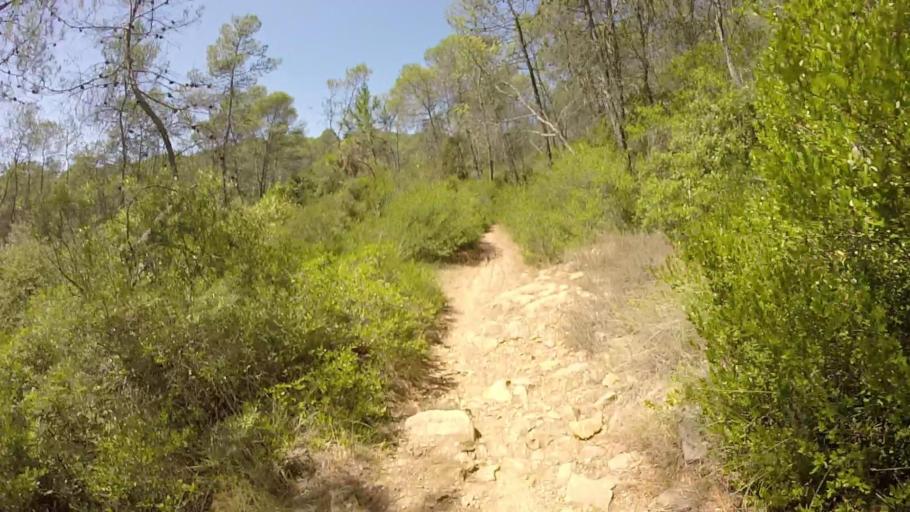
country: FR
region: Provence-Alpes-Cote d'Azur
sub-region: Departement des Alpes-Maritimes
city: Vallauris
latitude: 43.6074
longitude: 7.0495
